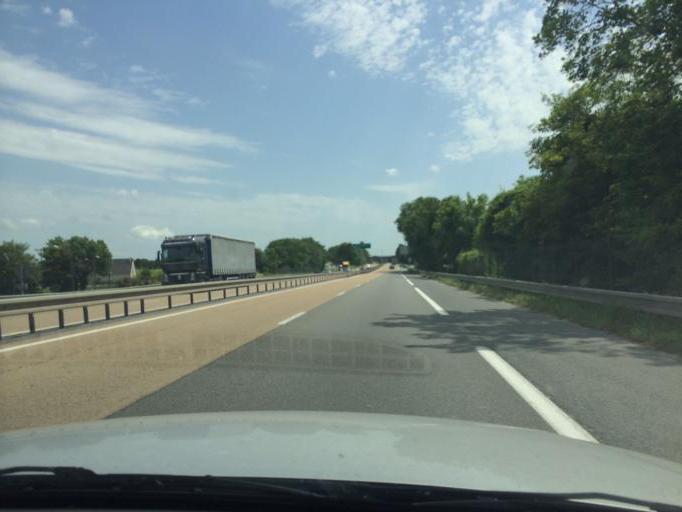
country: FR
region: Champagne-Ardenne
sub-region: Departement de la Marne
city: Saint-Memmie
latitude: 48.9539
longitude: 4.3899
